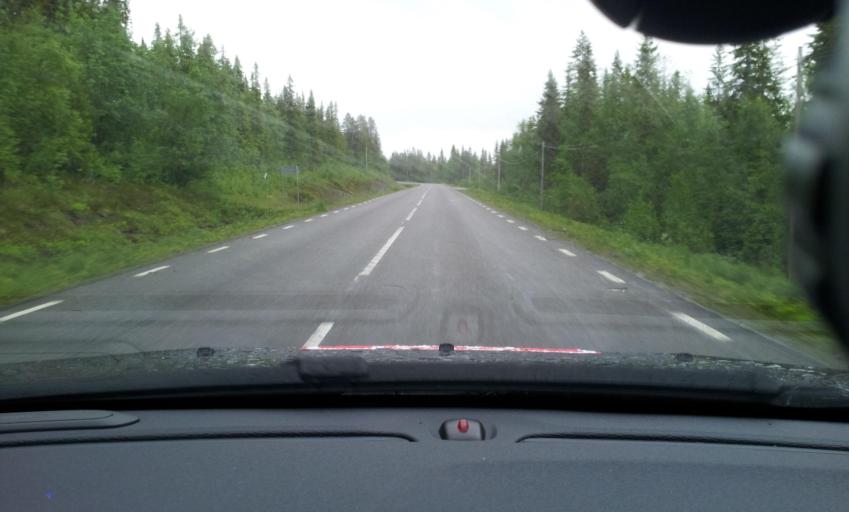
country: SE
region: Jaemtland
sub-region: Are Kommun
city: Are
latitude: 63.2157
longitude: 13.0645
